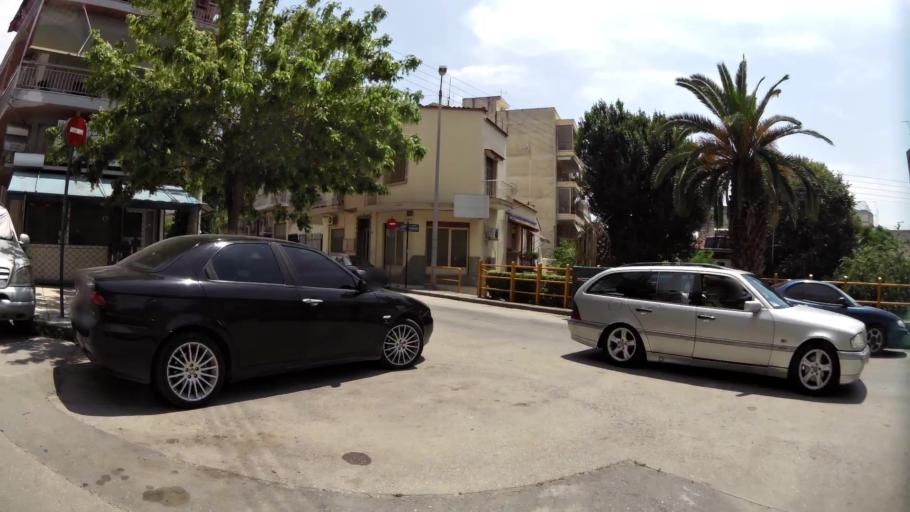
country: GR
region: Central Macedonia
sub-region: Nomos Thessalonikis
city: Ampelokipoi
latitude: 40.6508
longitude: 22.9316
